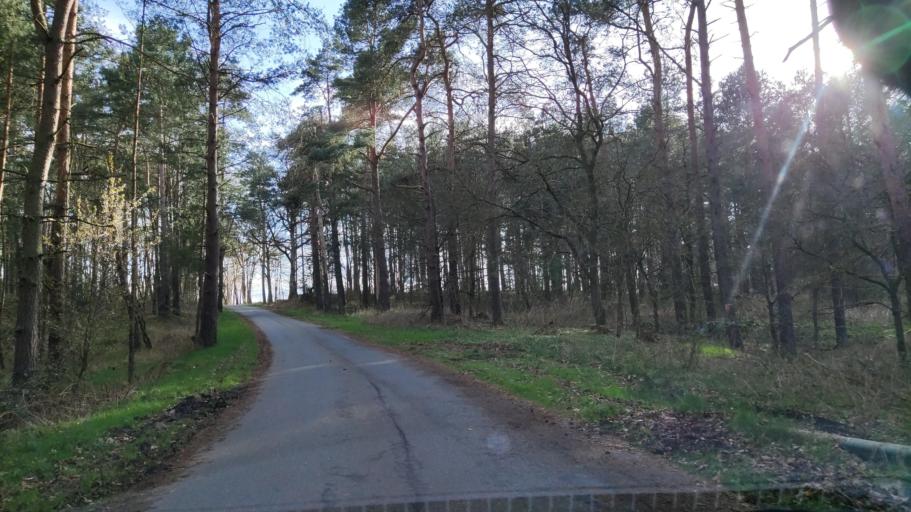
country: DE
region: Lower Saxony
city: Bienenbuttel
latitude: 53.1297
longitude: 10.5083
